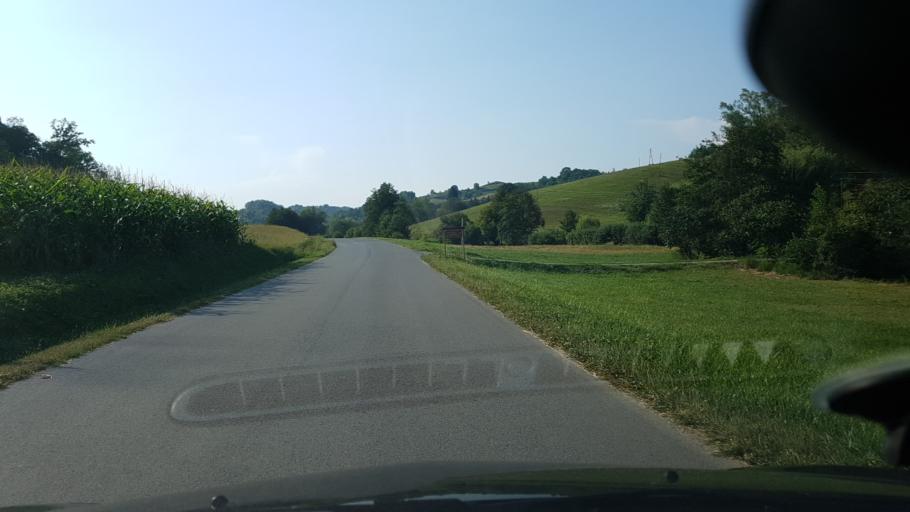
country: HR
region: Krapinsko-Zagorska
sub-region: Grad Krapina
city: Krapina
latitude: 46.1218
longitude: 15.8550
